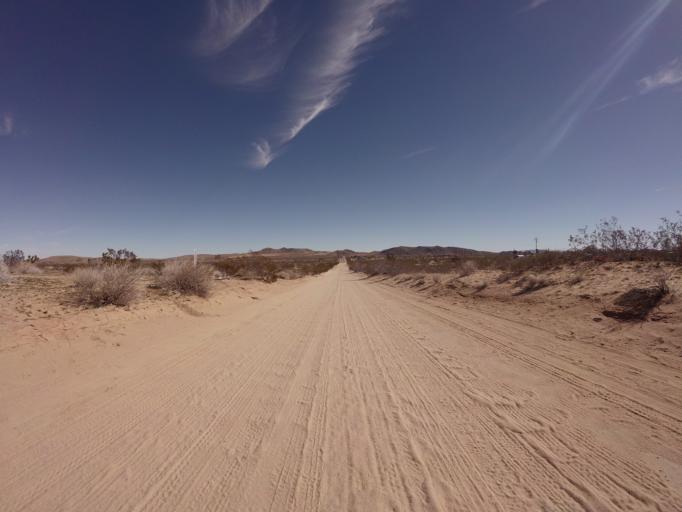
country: US
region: California
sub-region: San Bernardino County
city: Yucca Valley
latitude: 34.2370
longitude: -116.3969
